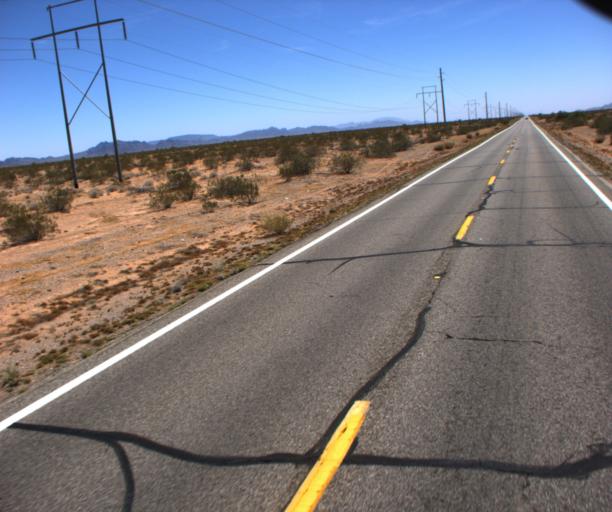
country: US
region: Arizona
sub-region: La Paz County
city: Quartzsite
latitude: 33.8740
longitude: -114.2170
